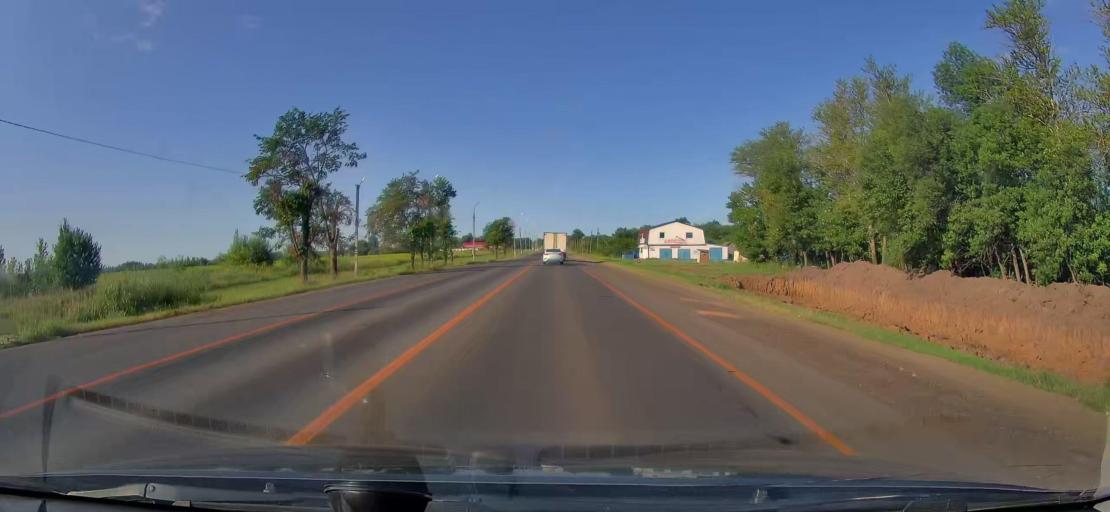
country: RU
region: Tula
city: Bol'shoye Skuratovo
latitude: 53.4024
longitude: 36.7656
